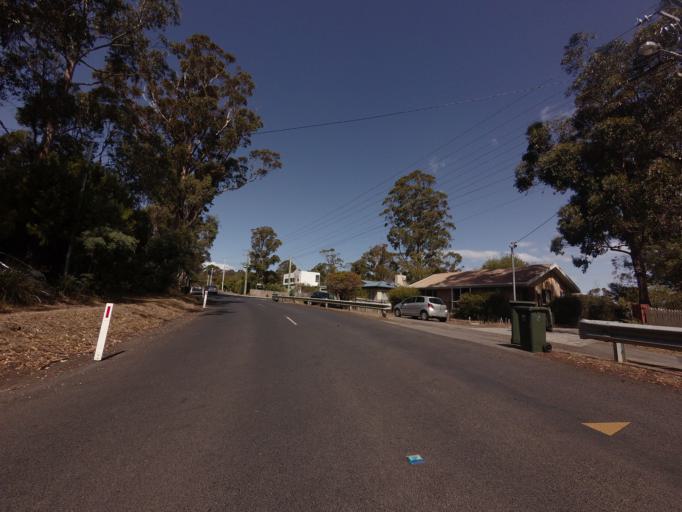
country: AU
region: Tasmania
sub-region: Hobart
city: Dynnyrne
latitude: -42.9233
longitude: 147.3245
